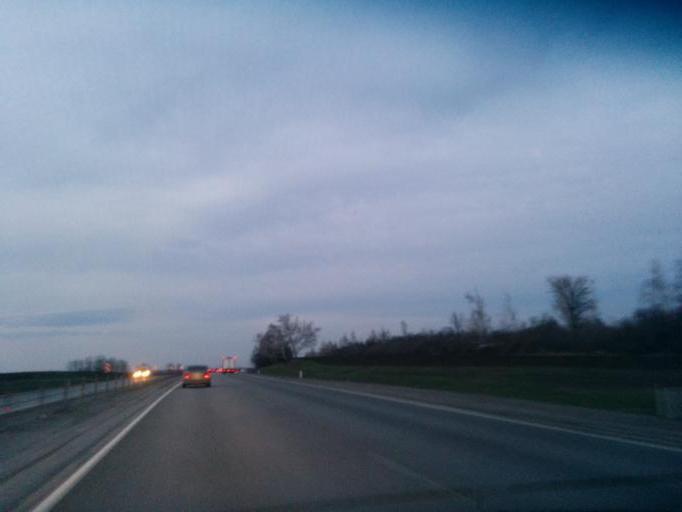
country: RU
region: Rostov
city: Grushevskaya
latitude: 47.5718
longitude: 39.9685
